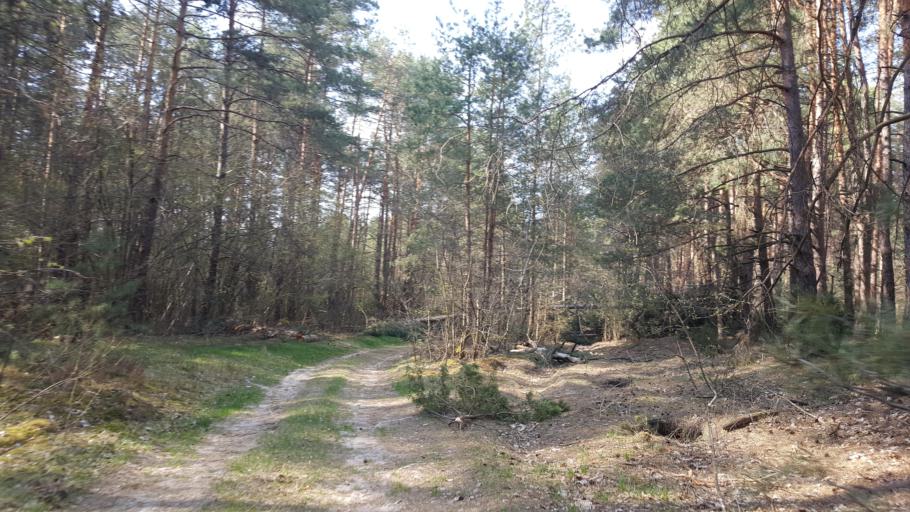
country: BY
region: Brest
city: Kamyanyets
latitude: 52.3400
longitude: 23.8490
